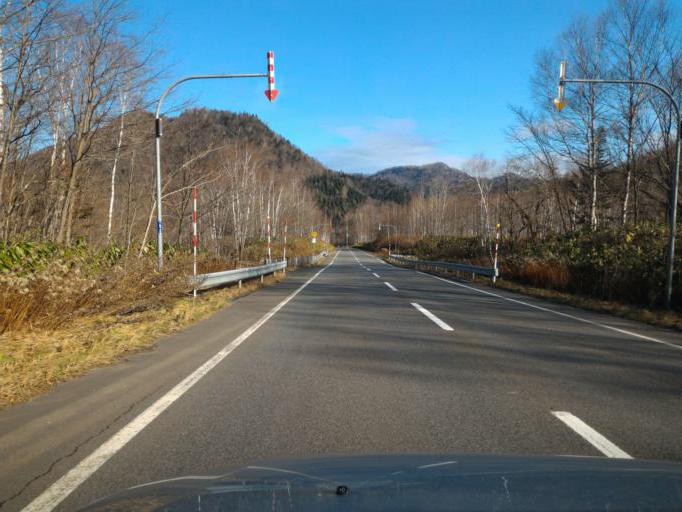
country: JP
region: Hokkaido
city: Ashibetsu
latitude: 43.3246
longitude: 142.1516
